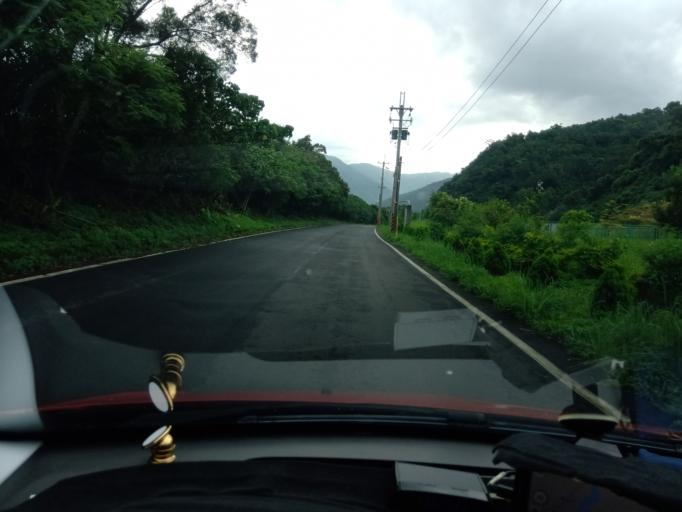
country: TW
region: Taiwan
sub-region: Yilan
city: Yilan
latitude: 24.7811
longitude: 121.7101
